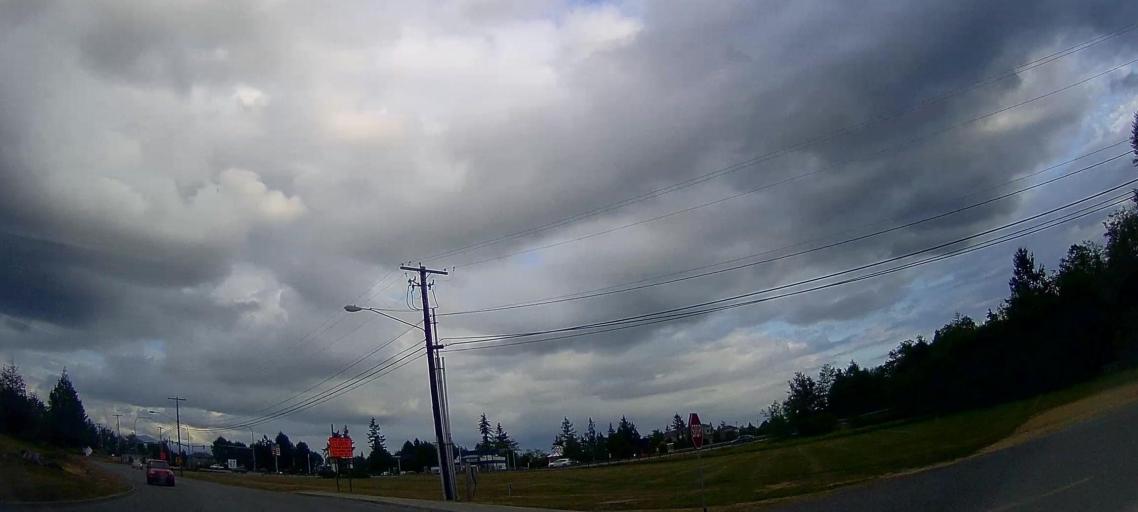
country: US
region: Washington
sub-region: Skagit County
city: Burlington
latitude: 48.5579
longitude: -122.3452
